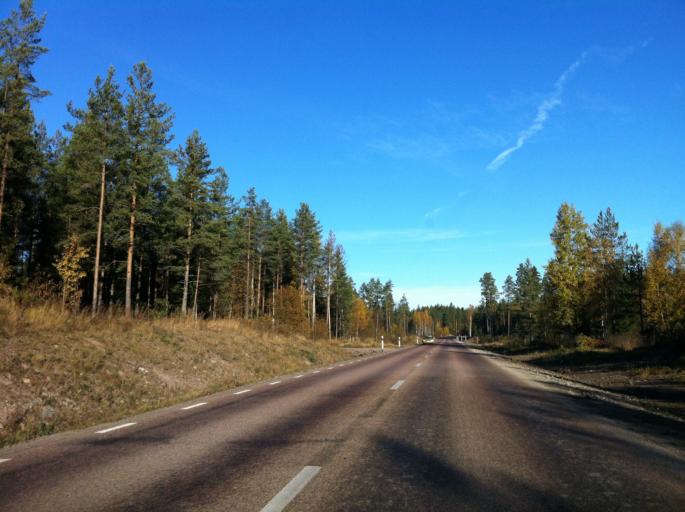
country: SE
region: Gaevleborg
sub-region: Gavle Kommun
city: Gavle
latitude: 60.6097
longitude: 17.1199
